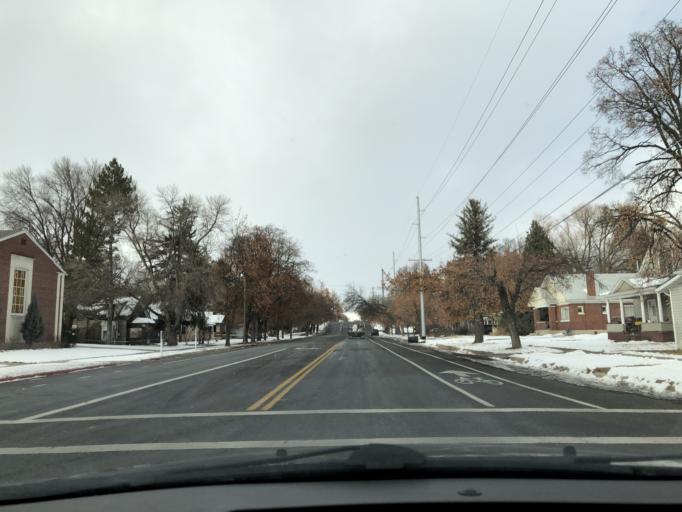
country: US
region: Utah
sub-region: Cache County
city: Logan
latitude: 41.7276
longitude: -111.8325
